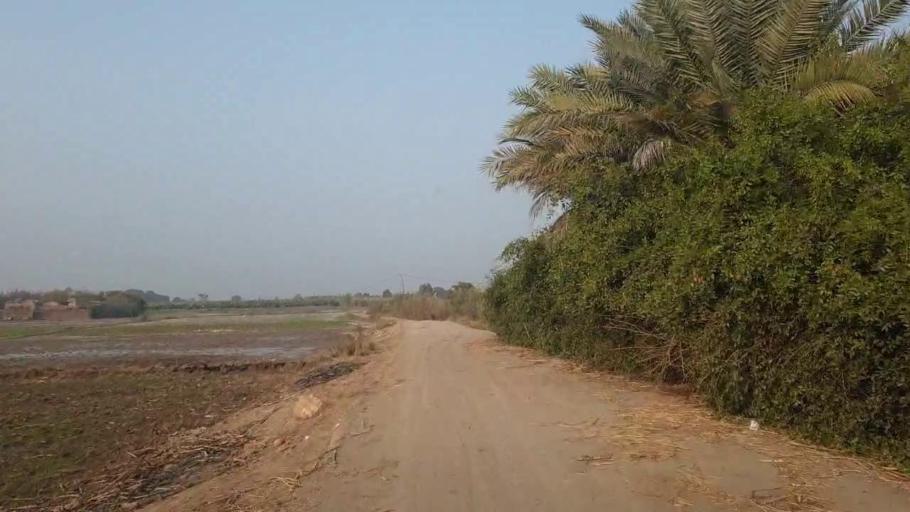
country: PK
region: Sindh
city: Shahdadpur
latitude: 25.8781
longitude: 68.6041
